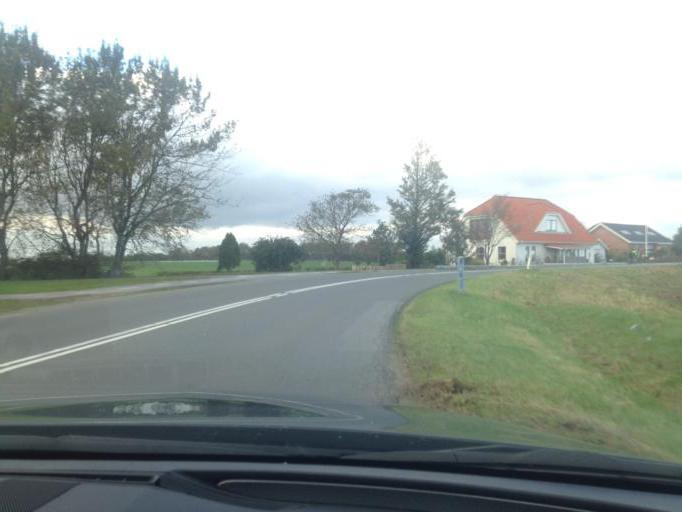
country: DK
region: South Denmark
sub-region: Kolding Kommune
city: Kolding
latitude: 55.5567
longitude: 9.4855
